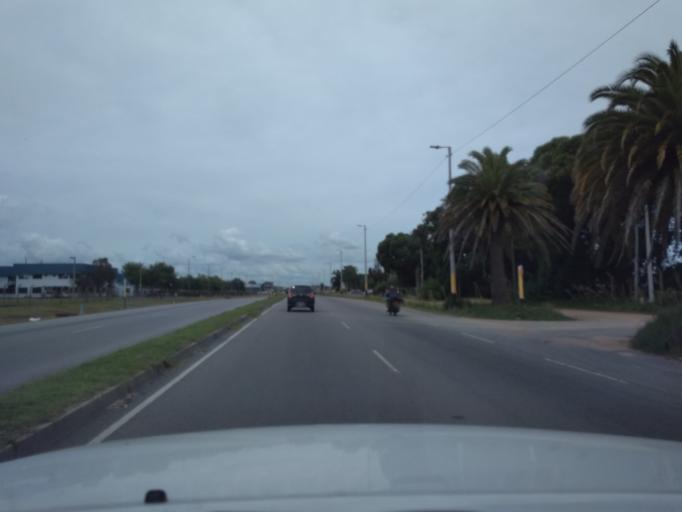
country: UY
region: Canelones
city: Paso de Carrasco
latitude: -34.8477
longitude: -56.0304
